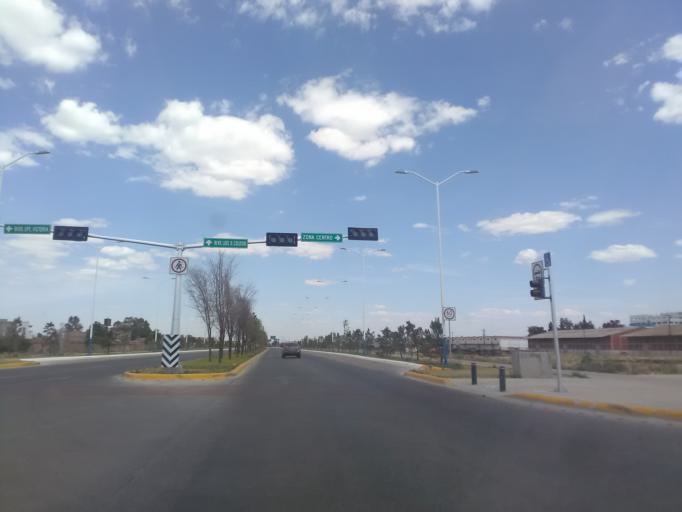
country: MX
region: Durango
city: Victoria de Durango
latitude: 24.0367
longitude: -104.6663
